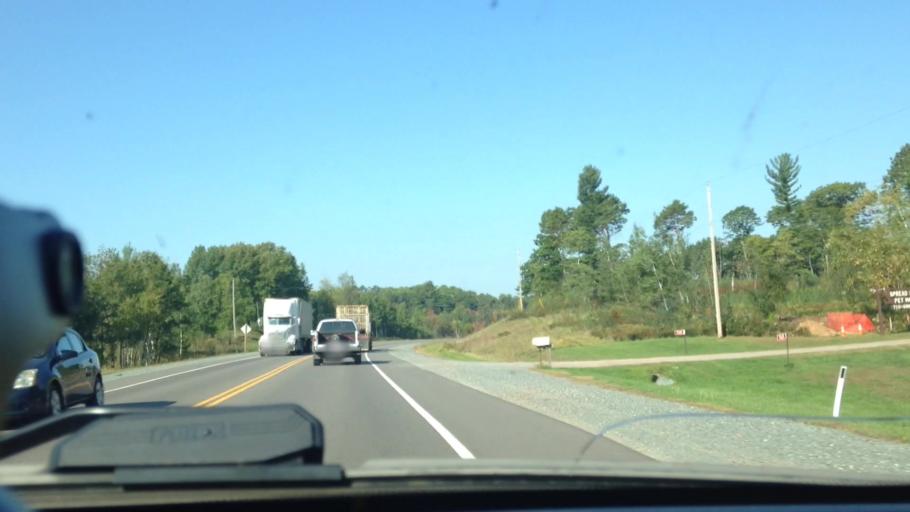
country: US
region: Michigan
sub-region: Dickinson County
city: Iron Mountain
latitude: 45.8760
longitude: -88.1115
